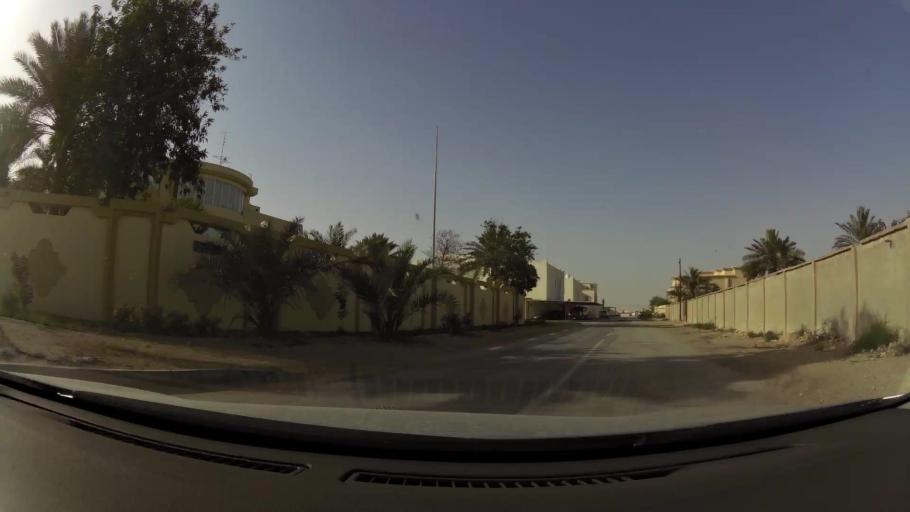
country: QA
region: Baladiyat ar Rayyan
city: Ar Rayyan
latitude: 25.3294
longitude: 51.4285
